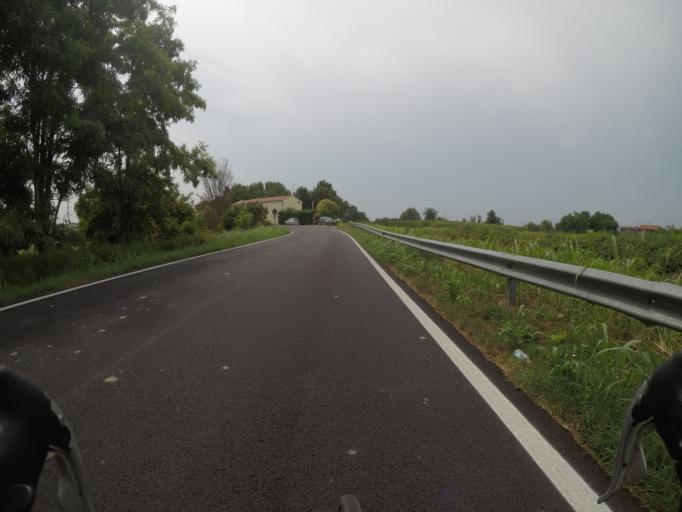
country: IT
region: Veneto
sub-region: Provincia di Rovigo
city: Costa di Rovigo
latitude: 45.0504
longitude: 11.6737
